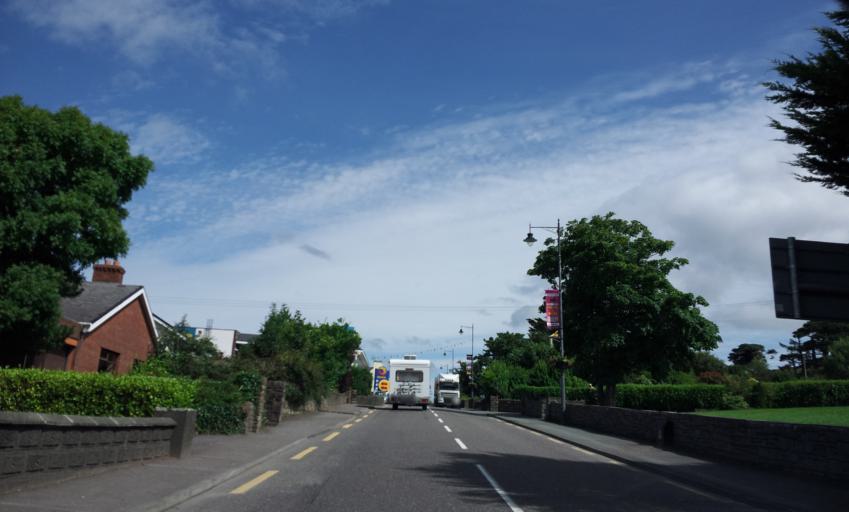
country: IE
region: Munster
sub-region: Ciarrai
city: Killorglin
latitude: 52.0552
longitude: -9.9435
